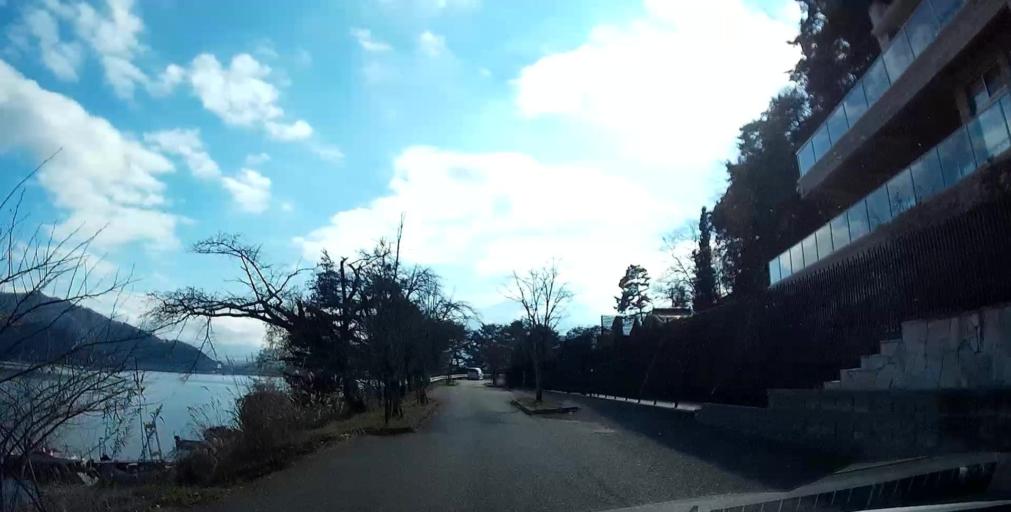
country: JP
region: Yamanashi
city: Fujikawaguchiko
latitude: 35.5228
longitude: 138.7576
